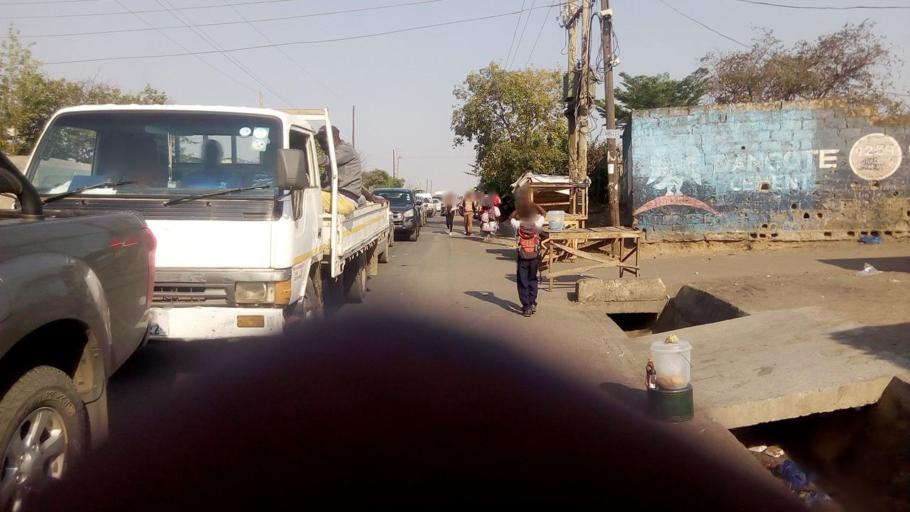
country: ZM
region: Lusaka
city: Lusaka
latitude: -15.3708
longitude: 28.2924
